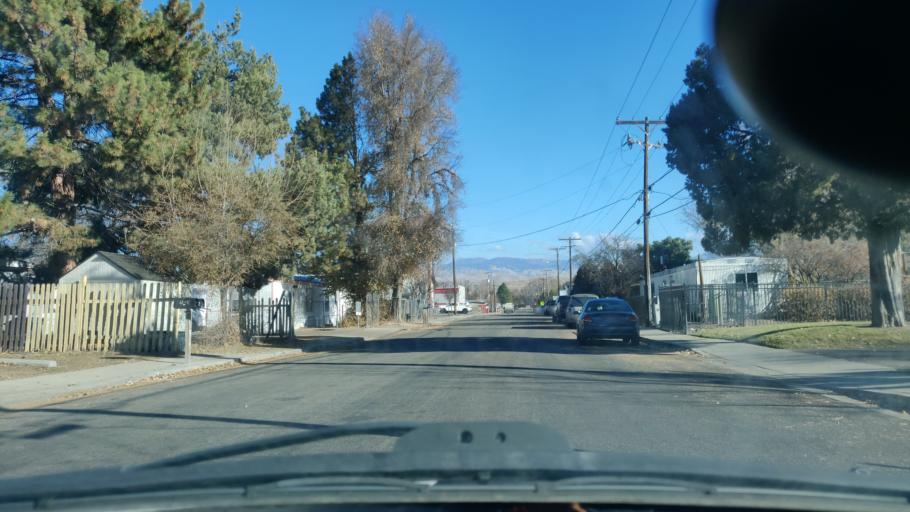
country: US
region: Idaho
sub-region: Ada County
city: Garden City
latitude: 43.6359
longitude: -116.2486
